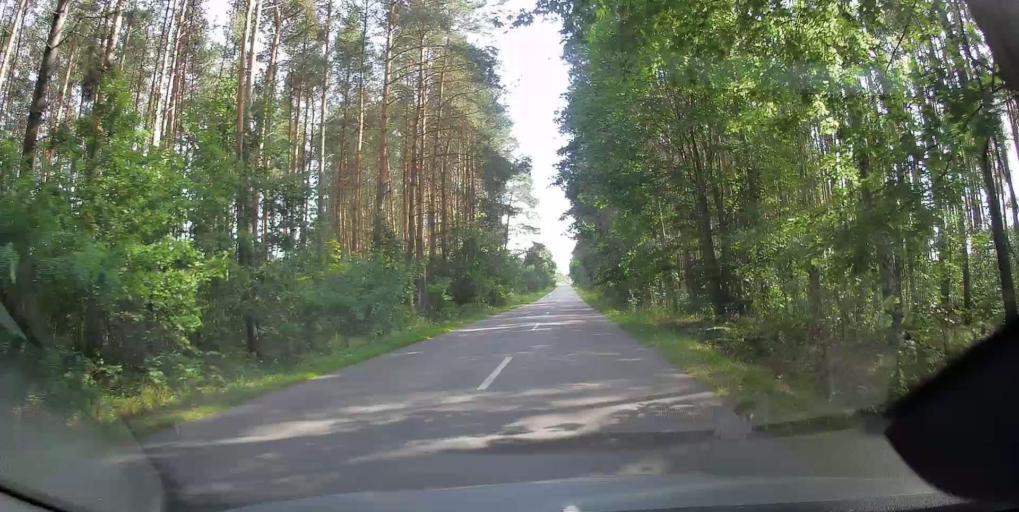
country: PL
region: Lodz Voivodeship
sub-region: Powiat opoczynski
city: Mniszkow
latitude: 51.3931
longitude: 20.0360
